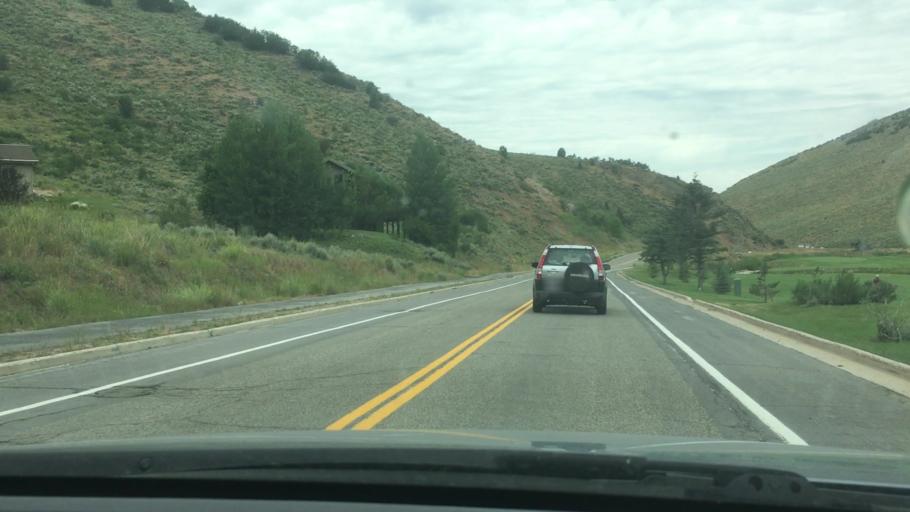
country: US
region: Utah
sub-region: Summit County
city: Summit Park
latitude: 40.7655
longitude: -111.5827
